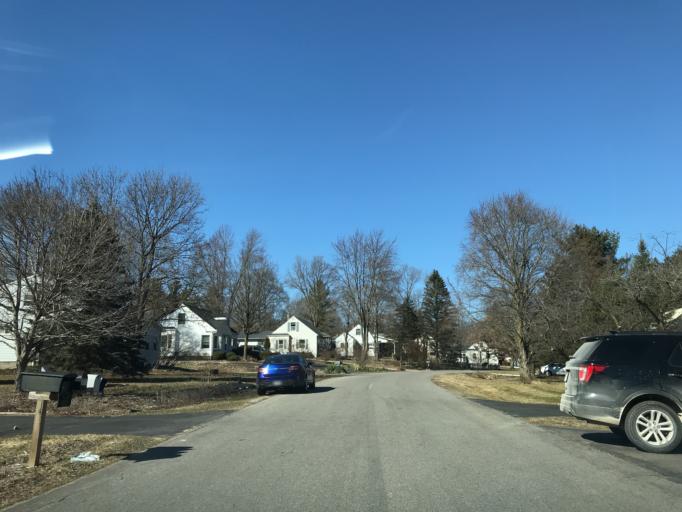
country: US
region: Michigan
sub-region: Washtenaw County
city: Ypsilanti
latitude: 42.3144
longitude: -83.6598
